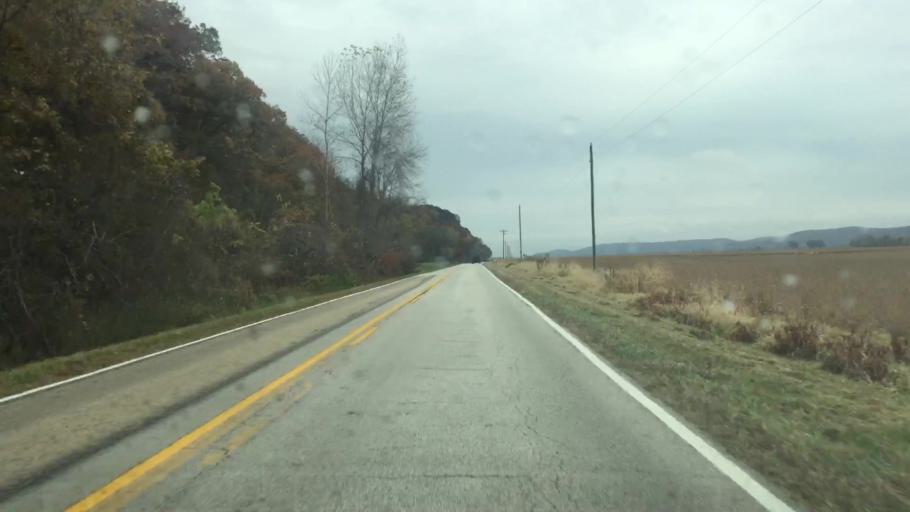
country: US
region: Missouri
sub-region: Gasconade County
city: Hermann
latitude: 38.7023
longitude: -91.5847
